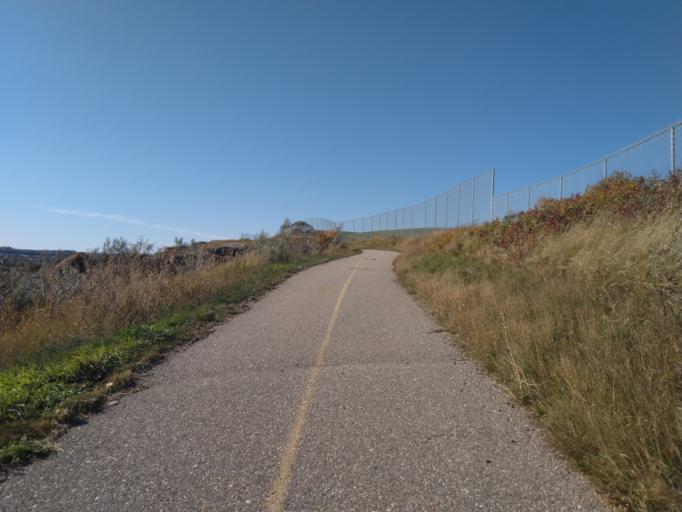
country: CA
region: Alberta
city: Calgary
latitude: 51.1496
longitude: -114.0910
